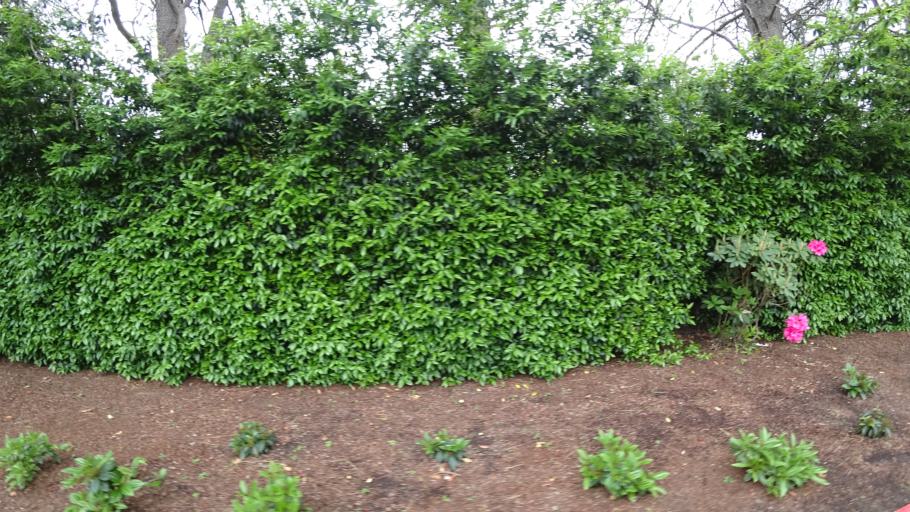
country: US
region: Oregon
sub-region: Washington County
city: Raleigh Hills
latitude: 45.4750
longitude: -122.7578
